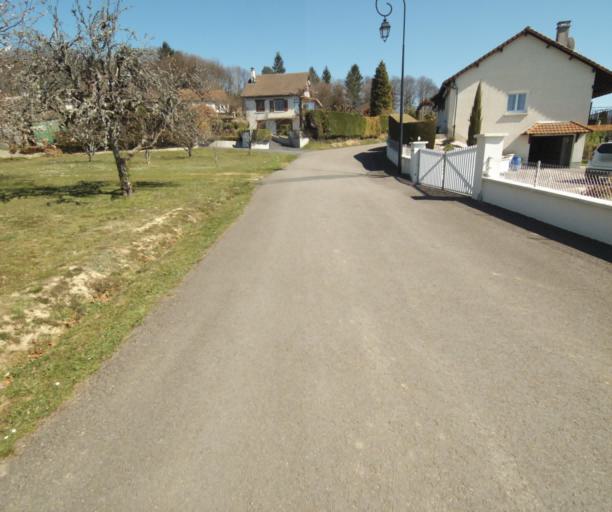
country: FR
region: Limousin
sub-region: Departement de la Correze
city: Saint-Mexant
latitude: 45.2793
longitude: 1.6618
